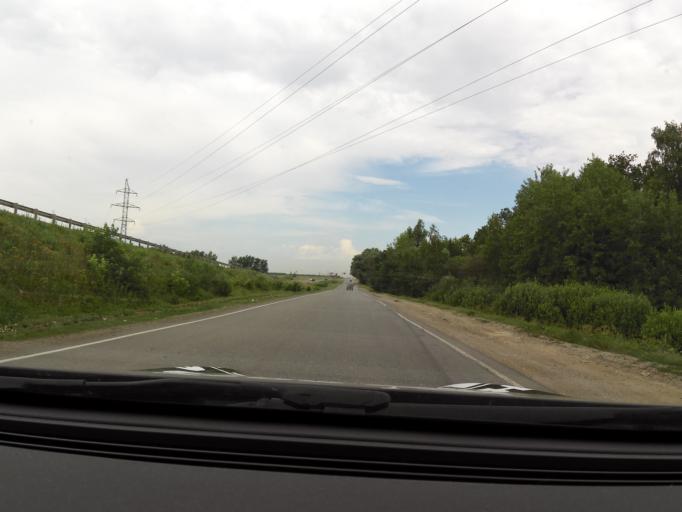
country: RU
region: Bashkortostan
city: Iglino
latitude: 54.7439
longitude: 56.3030
